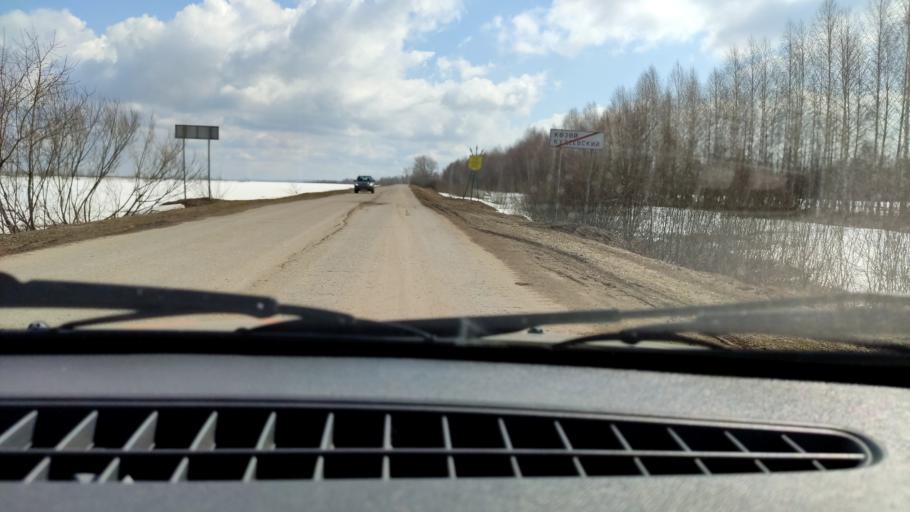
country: RU
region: Bashkortostan
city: Kudeyevskiy
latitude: 54.8648
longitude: 56.7480
